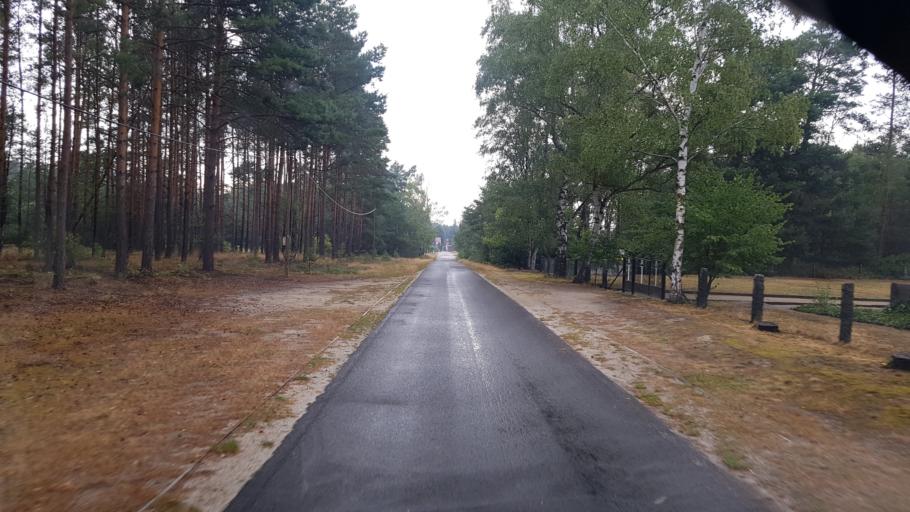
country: DE
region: Brandenburg
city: Finsterwalde
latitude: 51.6547
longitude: 13.7820
